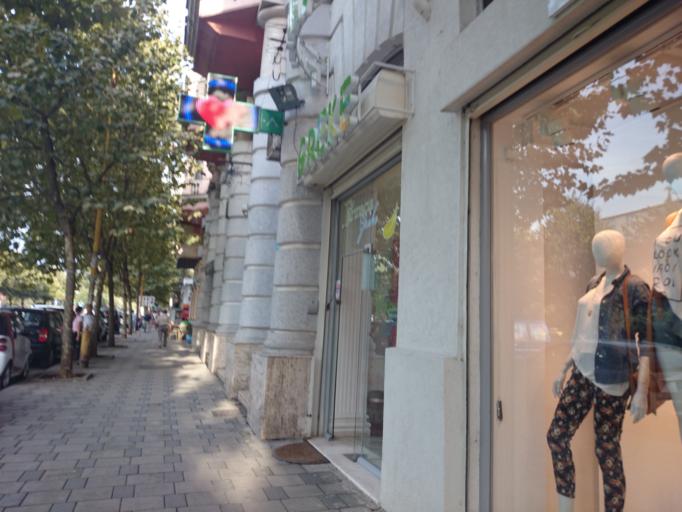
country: AL
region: Tirane
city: Tirana
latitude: 41.3228
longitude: 19.8162
